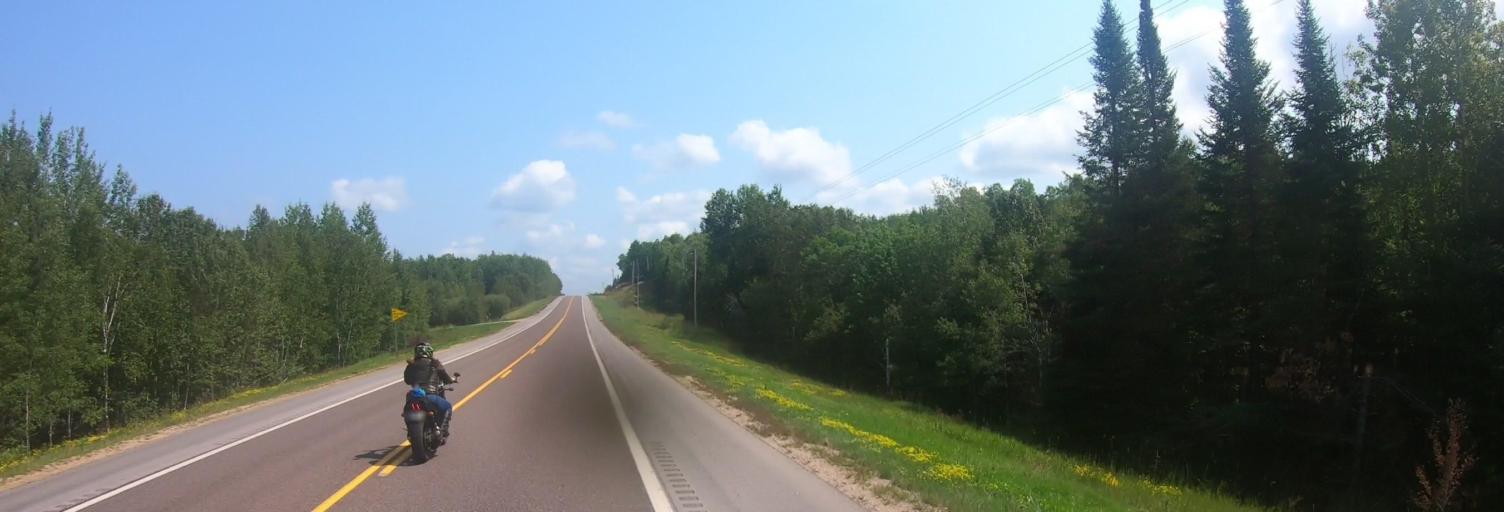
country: US
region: Minnesota
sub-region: Saint Louis County
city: Mountain Iron
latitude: 48.0728
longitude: -92.6861
